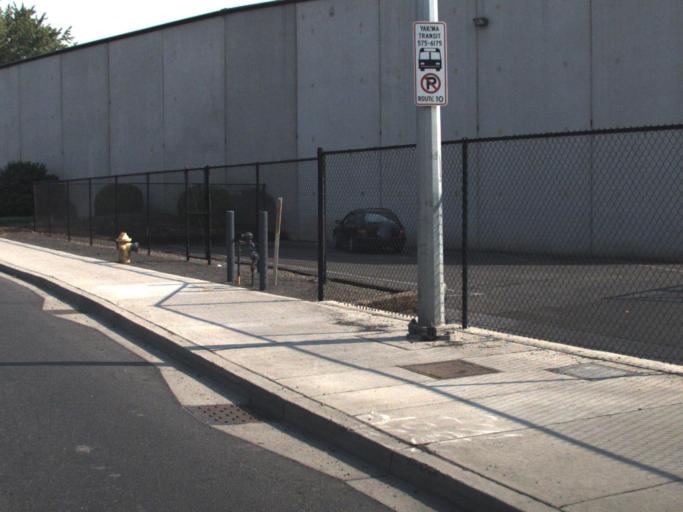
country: US
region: Washington
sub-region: Yakima County
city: Selah
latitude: 46.6565
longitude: -120.5268
